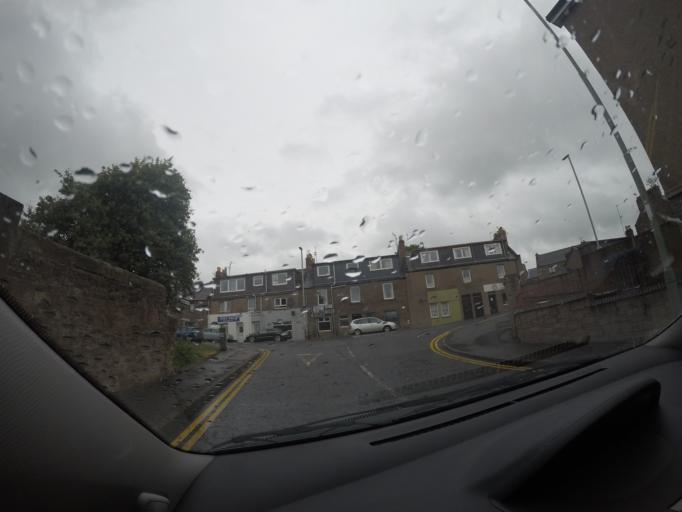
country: GB
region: Scotland
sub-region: Angus
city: Brechin
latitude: 56.7286
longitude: -2.6525
